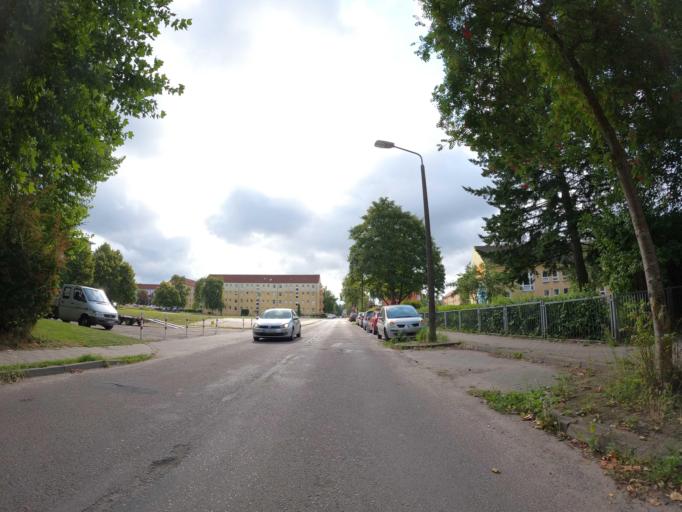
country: DE
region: Mecklenburg-Vorpommern
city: Stralsund
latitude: 54.3275
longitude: 13.0692
